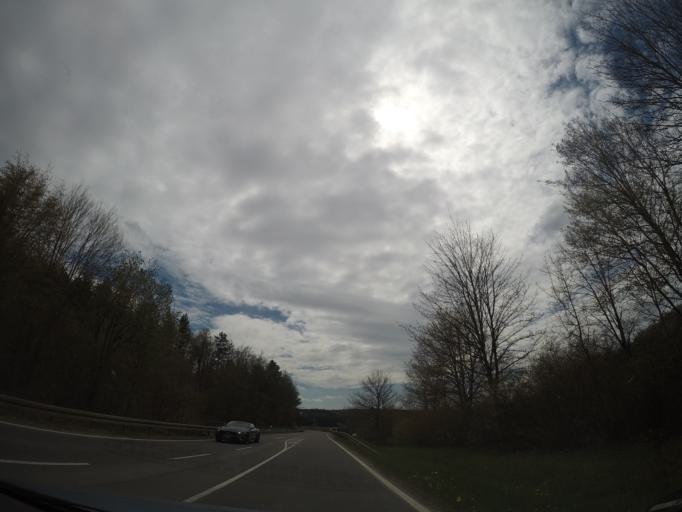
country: DE
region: Baden-Wuerttemberg
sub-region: Tuebingen Region
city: Laichingen
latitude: 48.4792
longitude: 9.6845
